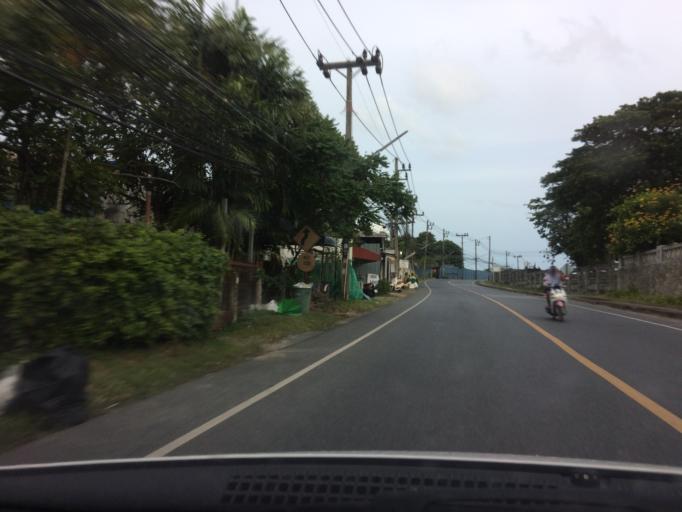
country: TH
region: Phuket
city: Ban Ratsada
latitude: 7.9036
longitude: 98.4098
